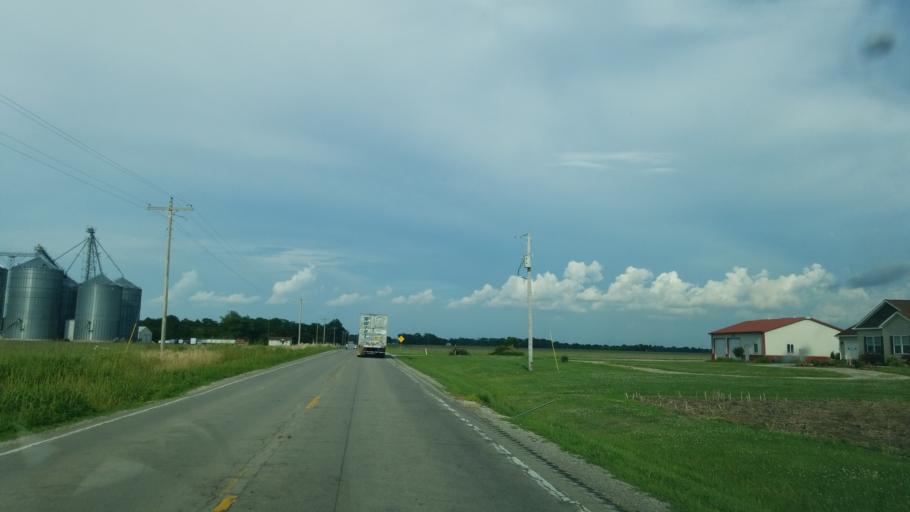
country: US
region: Illinois
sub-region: Marion County
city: Sandoval
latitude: 38.6165
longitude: -89.1548
